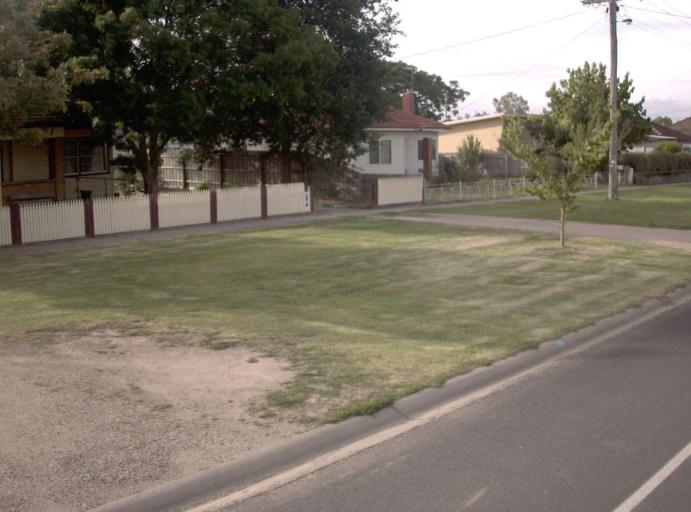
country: AU
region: Victoria
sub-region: Wellington
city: Sale
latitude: -37.9613
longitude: 146.9860
